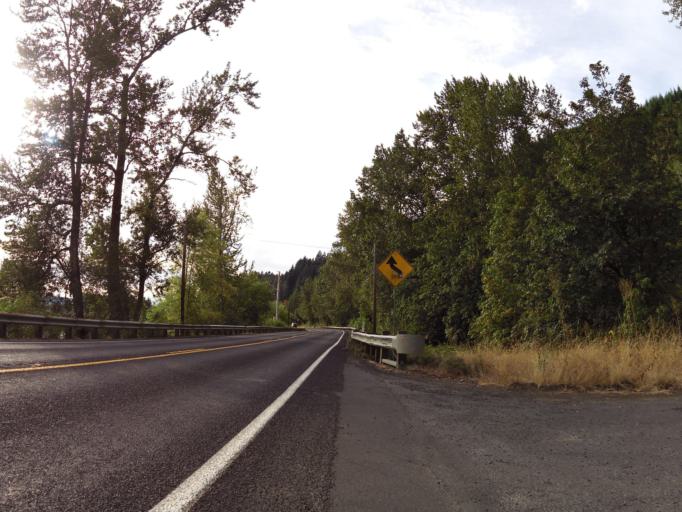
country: US
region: Washington
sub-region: Cowlitz County
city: West Longview
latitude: 46.1866
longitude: -123.0854
